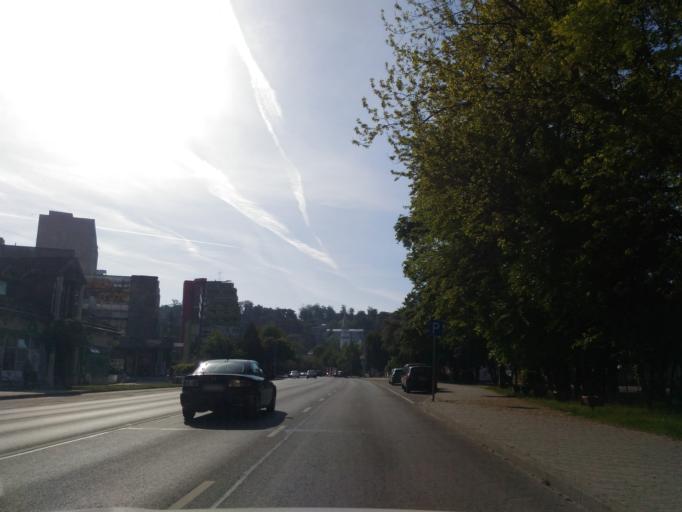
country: HU
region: Baranya
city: Komlo
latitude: 46.1902
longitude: 18.2647
